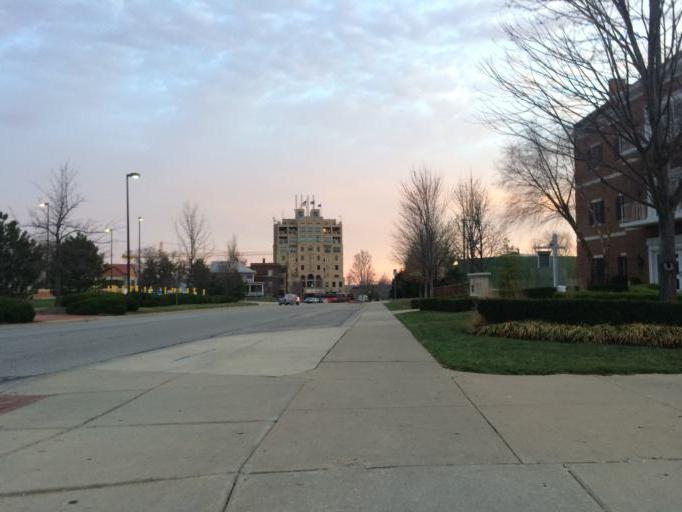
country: US
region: Kansas
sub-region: Douglas County
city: Lawrence
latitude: 38.9600
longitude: -95.2428
